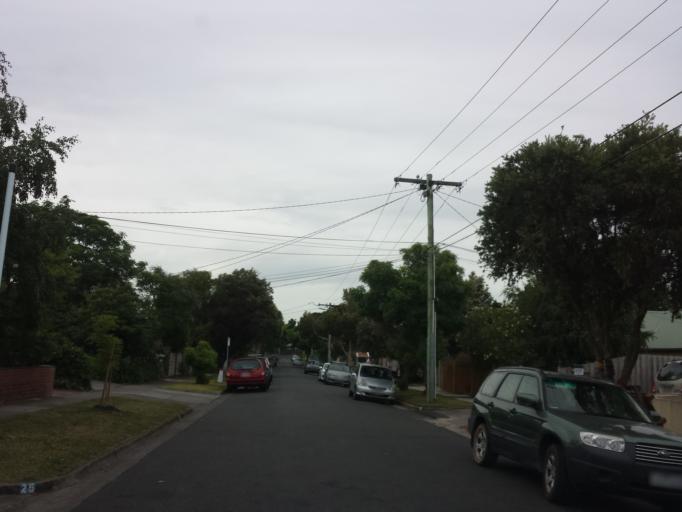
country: AU
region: Victoria
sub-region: Bayside
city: Highett
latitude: -37.9502
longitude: 145.0383
